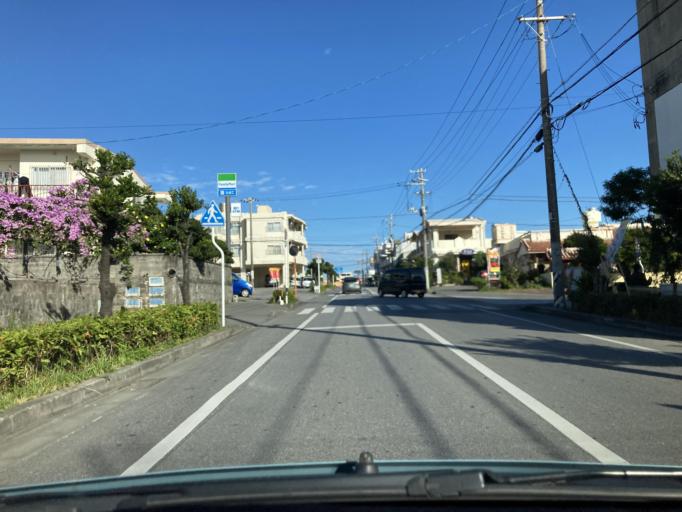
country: JP
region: Okinawa
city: Chatan
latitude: 26.3678
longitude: 127.7472
